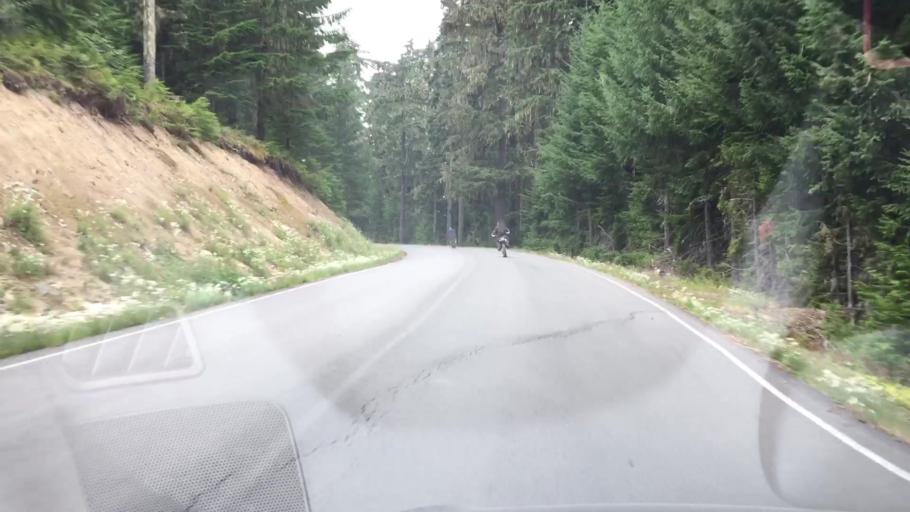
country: US
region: Washington
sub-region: Klickitat County
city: White Salmon
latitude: 46.2055
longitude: -121.6429
